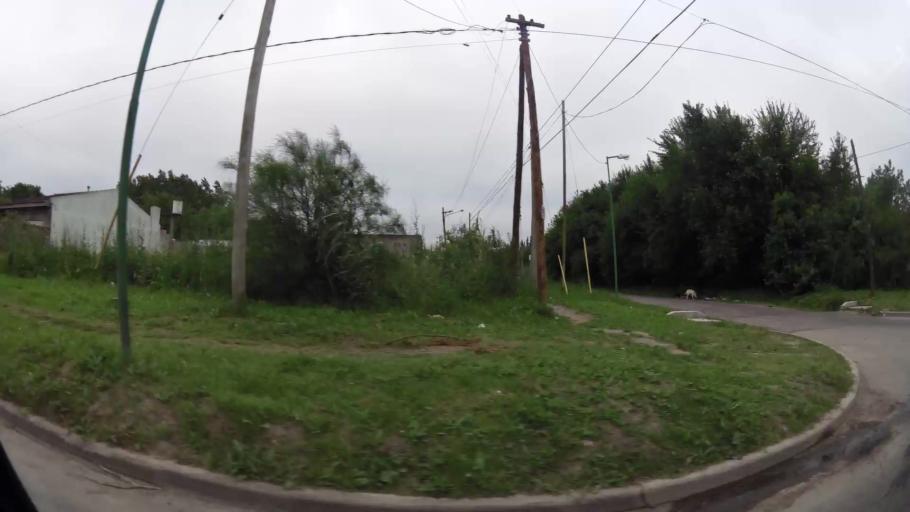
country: AR
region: Buenos Aires
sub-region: Partido de La Plata
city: La Plata
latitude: -34.9363
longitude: -58.0041
